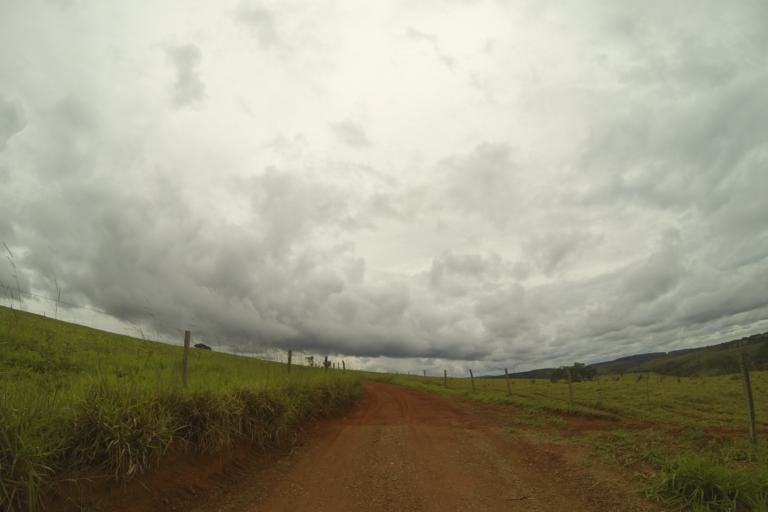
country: BR
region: Minas Gerais
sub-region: Ibia
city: Ibia
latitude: -19.7167
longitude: -46.5725
